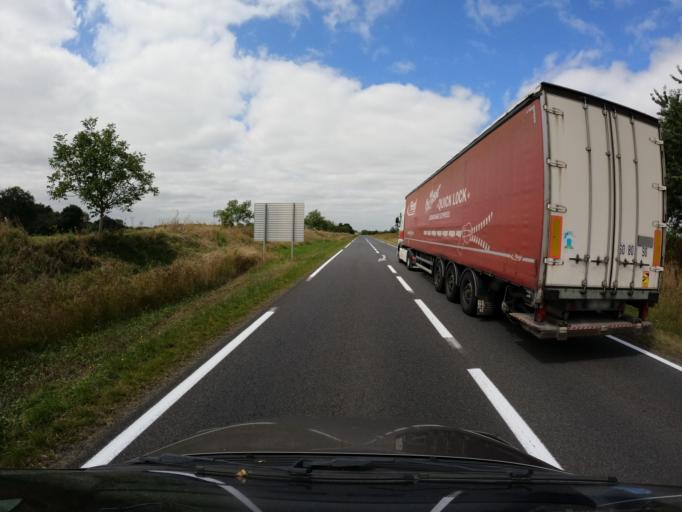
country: FR
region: Poitou-Charentes
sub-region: Departement de la Vienne
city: Charroux
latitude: 46.1511
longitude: 0.4042
